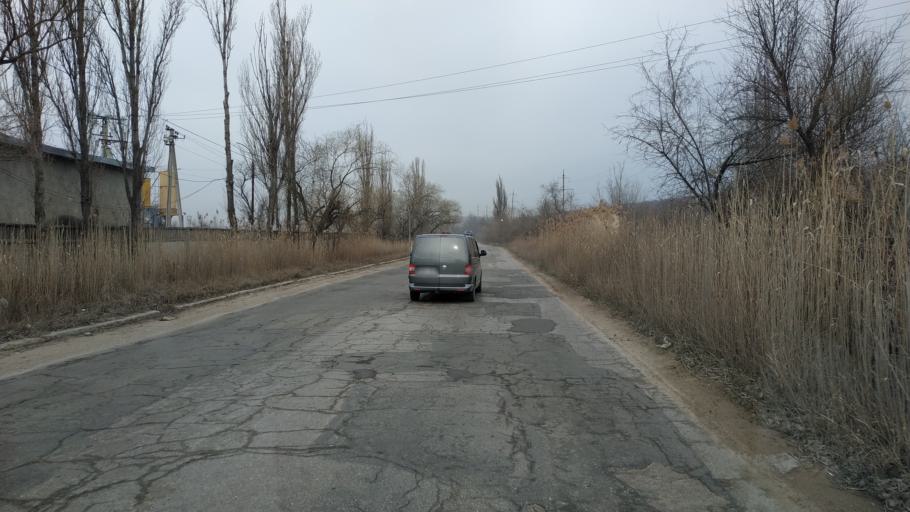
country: MD
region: Chisinau
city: Vatra
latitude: 47.0684
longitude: 28.7773
